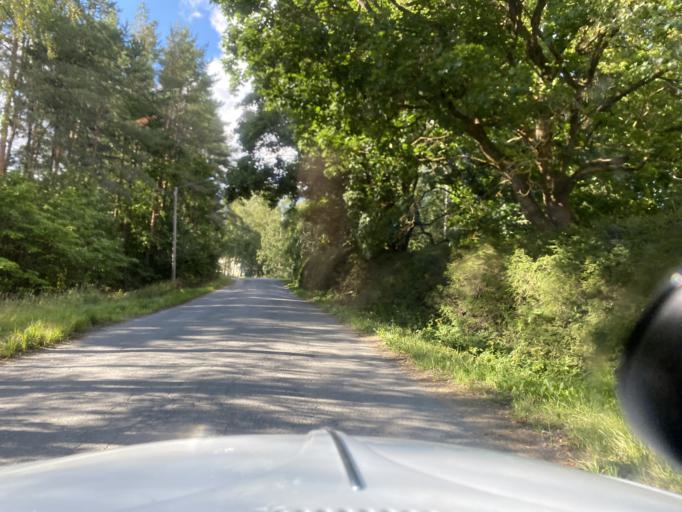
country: FI
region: Pirkanmaa
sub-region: Lounais-Pirkanmaa
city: Punkalaidun
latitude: 61.1463
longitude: 23.1967
